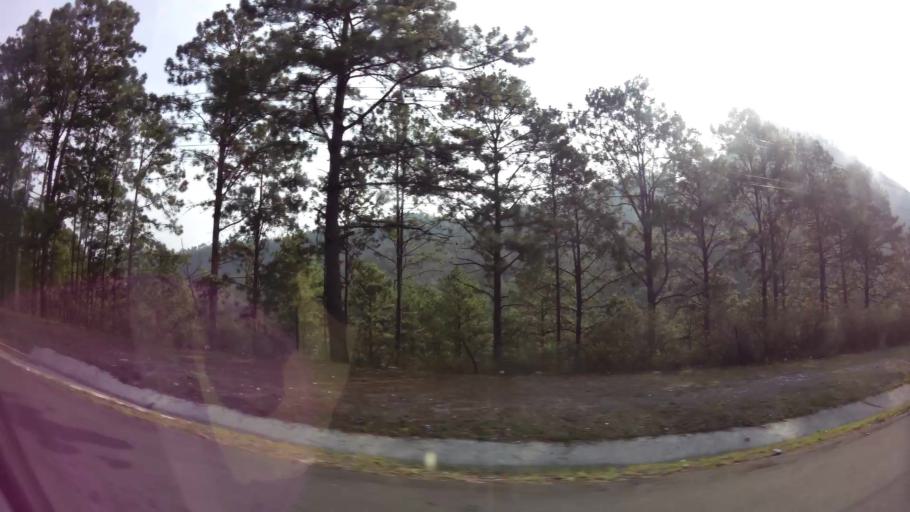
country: HN
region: Comayagua
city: Flores
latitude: 14.2921
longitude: -87.4820
